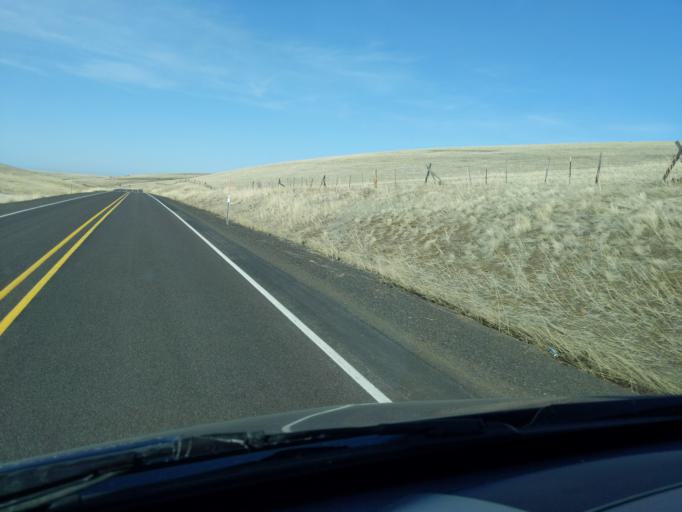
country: US
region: Oregon
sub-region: Umatilla County
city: Pilot Rock
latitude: 45.3228
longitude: -119.0055
